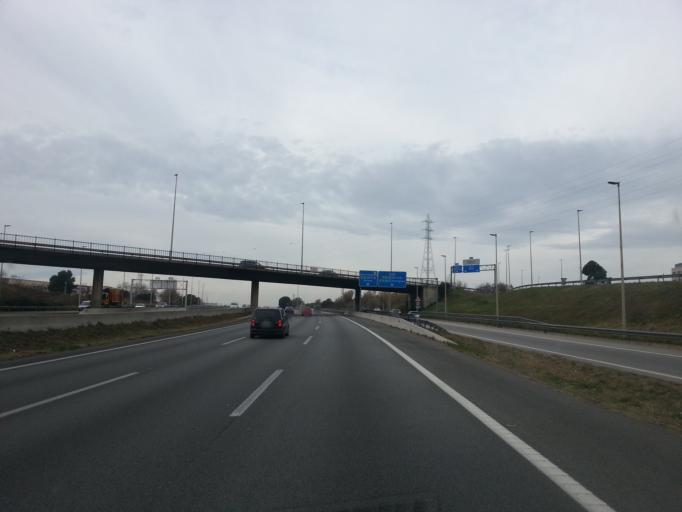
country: ES
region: Catalonia
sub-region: Provincia de Barcelona
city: Cerdanyola del Valles
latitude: 41.5050
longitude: 2.1381
